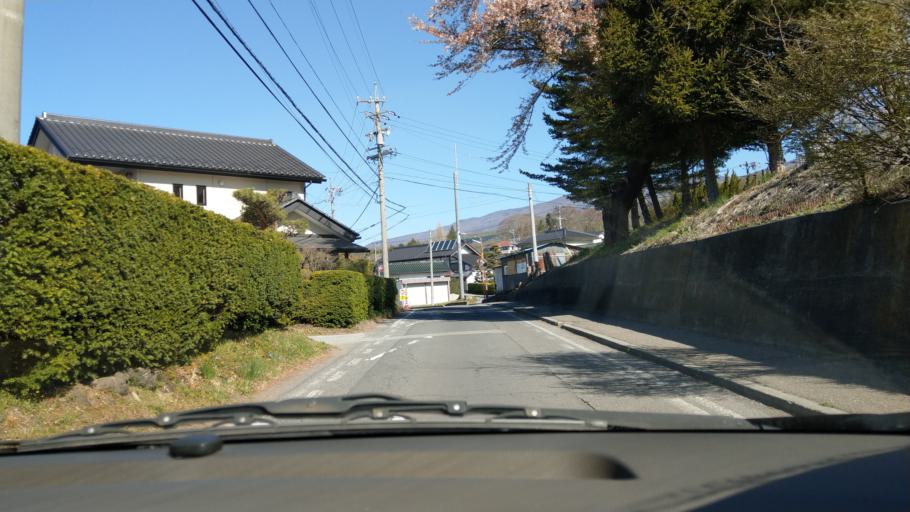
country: JP
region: Nagano
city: Komoro
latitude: 36.3339
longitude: 138.4978
